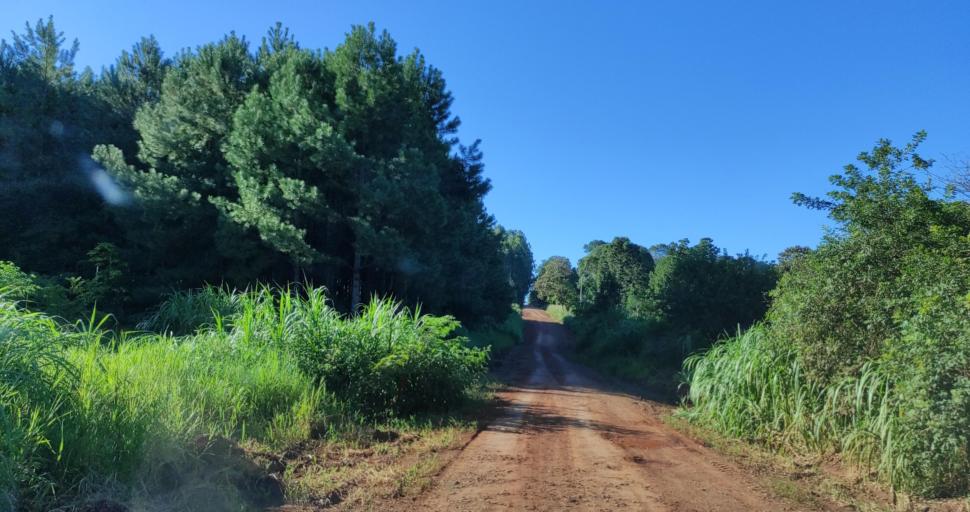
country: AR
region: Misiones
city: Garuhape
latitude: -26.8632
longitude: -55.0047
